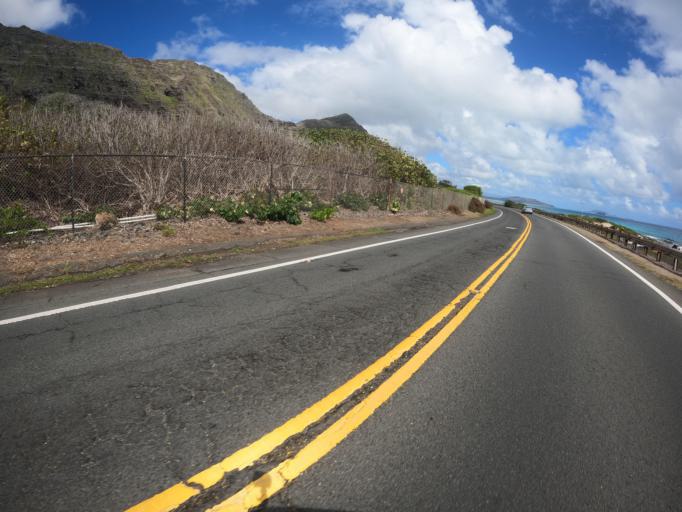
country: US
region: Hawaii
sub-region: Honolulu County
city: Waimanalo Beach
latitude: 21.3148
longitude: -157.6619
